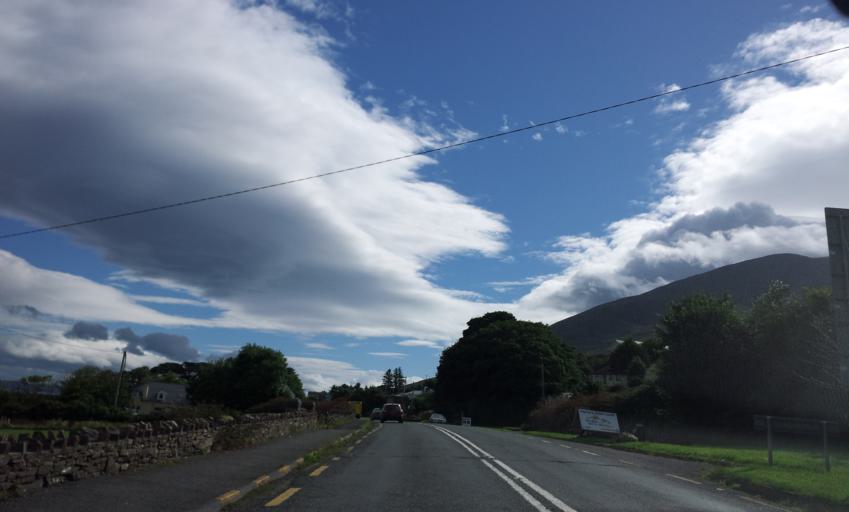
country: IE
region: Munster
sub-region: Ciarrai
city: Killorglin
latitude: 52.2261
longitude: -9.8943
